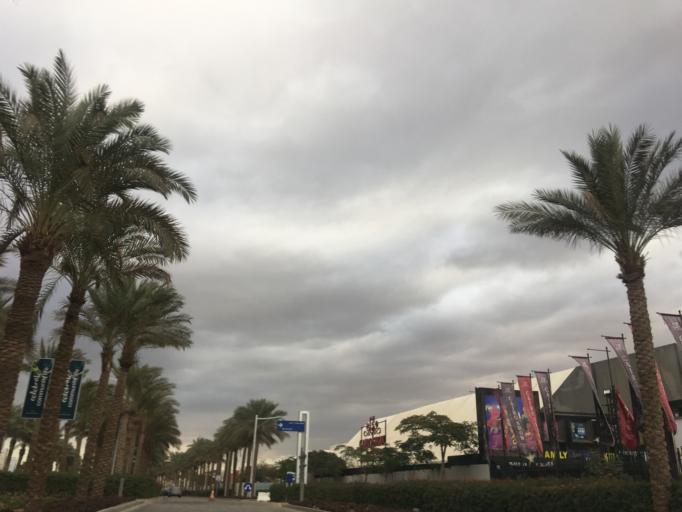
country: EG
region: Muhafazat al Qahirah
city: Cairo
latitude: 30.0298
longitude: 31.4108
